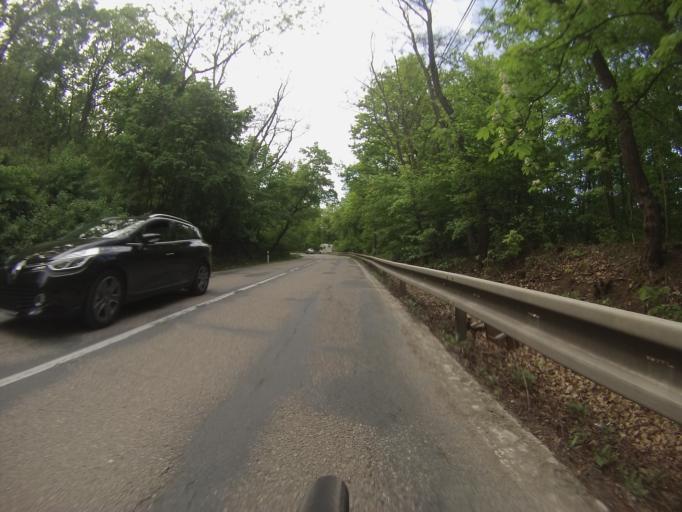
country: CZ
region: South Moravian
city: Kurim
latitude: 49.2466
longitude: 16.4956
